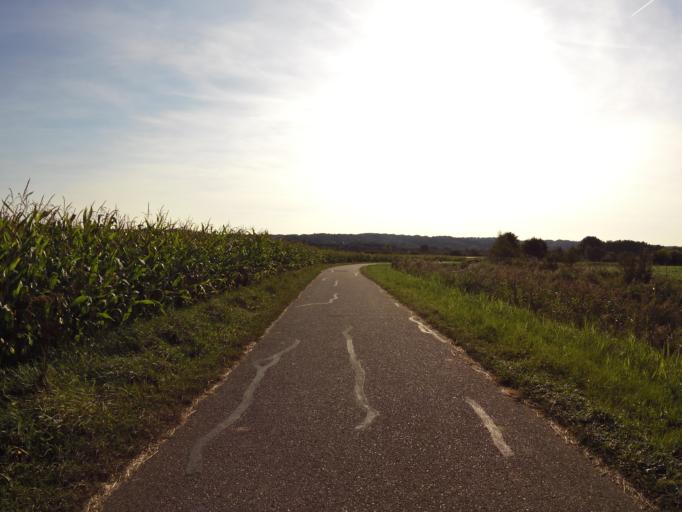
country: NL
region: Gelderland
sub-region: Gemeente Groesbeek
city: Berg en Dal
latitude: 51.8337
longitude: 5.9516
